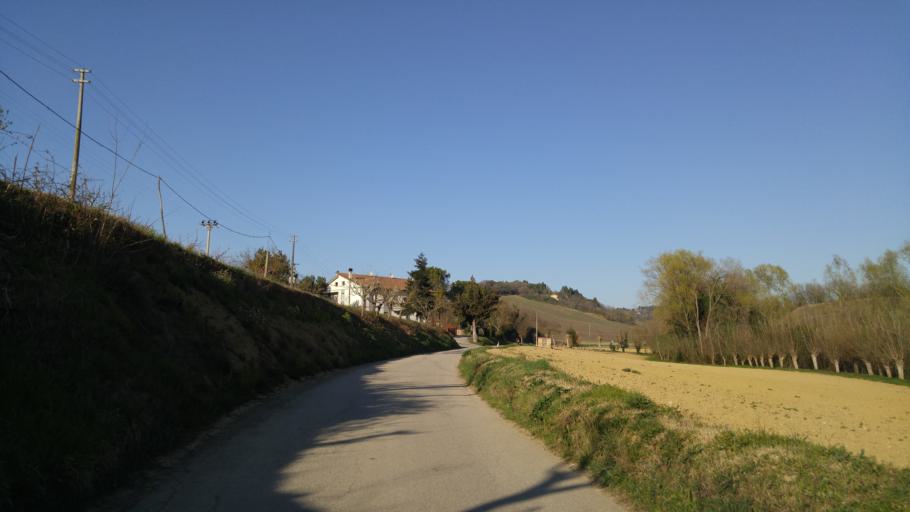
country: IT
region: The Marches
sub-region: Provincia di Pesaro e Urbino
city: Fenile
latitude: 43.8431
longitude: 12.9156
